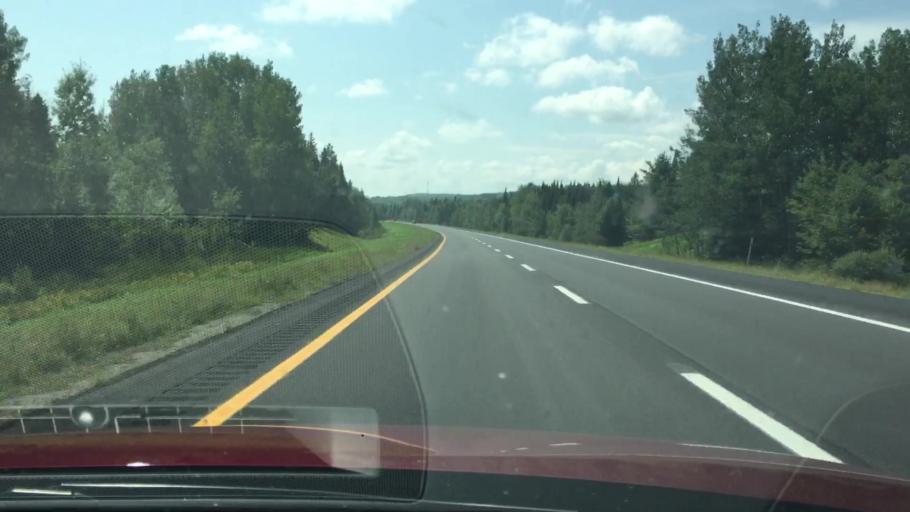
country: US
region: Maine
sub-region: Penobscot County
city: Patten
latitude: 45.8961
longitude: -68.3977
